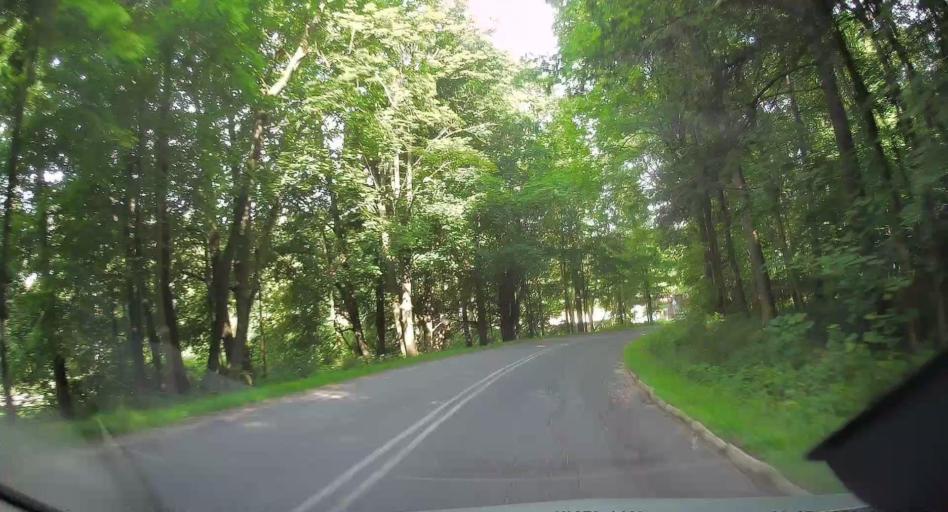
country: PL
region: Lower Silesian Voivodeship
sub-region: Powiat walbrzyski
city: Walim
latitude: 50.7294
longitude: 16.4061
